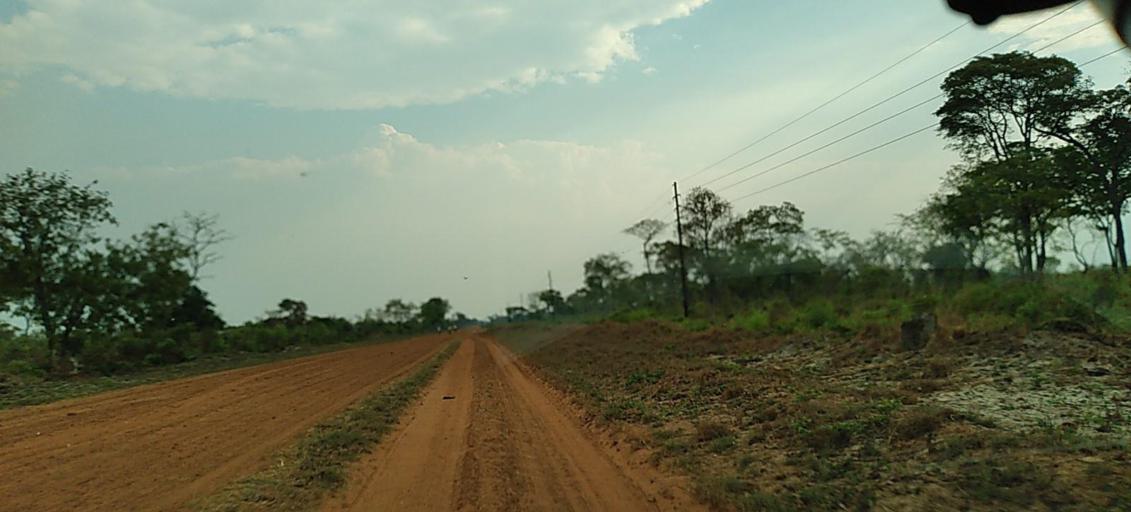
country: ZM
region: North-Western
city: Kabompo
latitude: -13.8885
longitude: 23.6607
